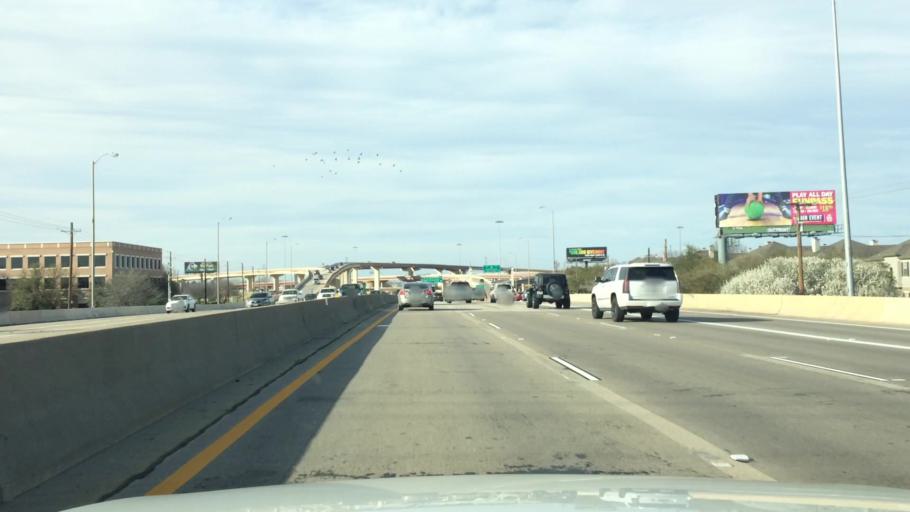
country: US
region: Texas
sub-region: Dallas County
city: Addison
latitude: 33.0073
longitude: -96.8292
